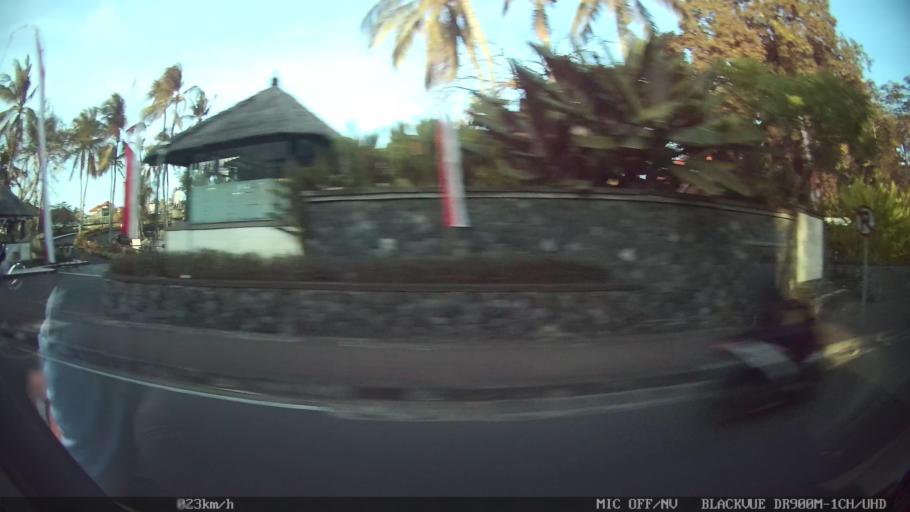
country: ID
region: Bali
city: Bualu
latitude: -8.7812
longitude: 115.2242
